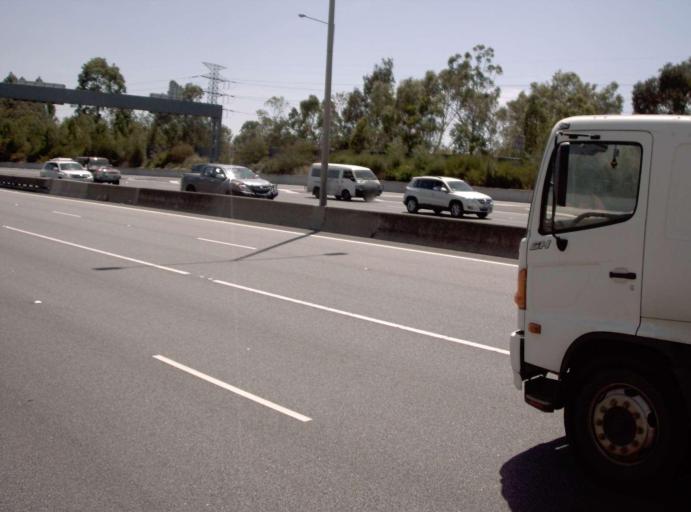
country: AU
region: Victoria
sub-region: Stonnington
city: Glen Iris
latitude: -37.8577
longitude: 145.0585
